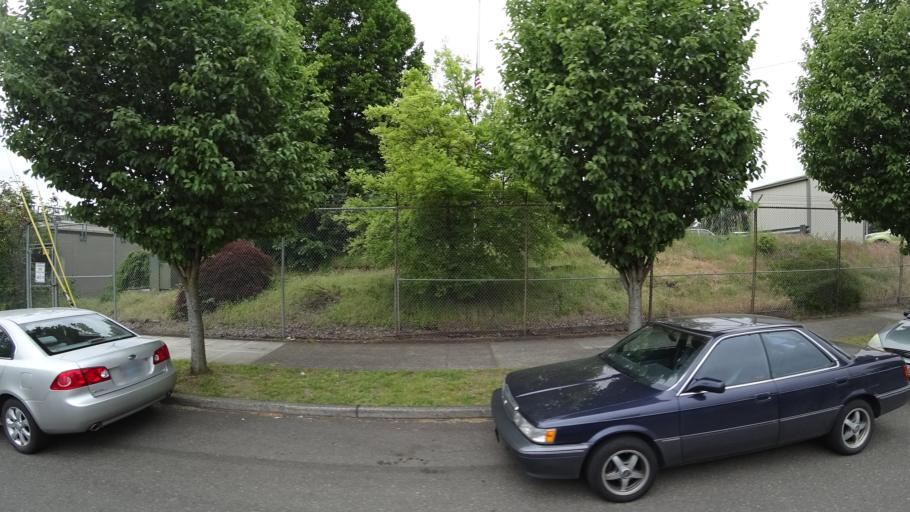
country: US
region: Oregon
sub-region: Multnomah County
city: Portland
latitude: 45.5445
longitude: -122.6721
